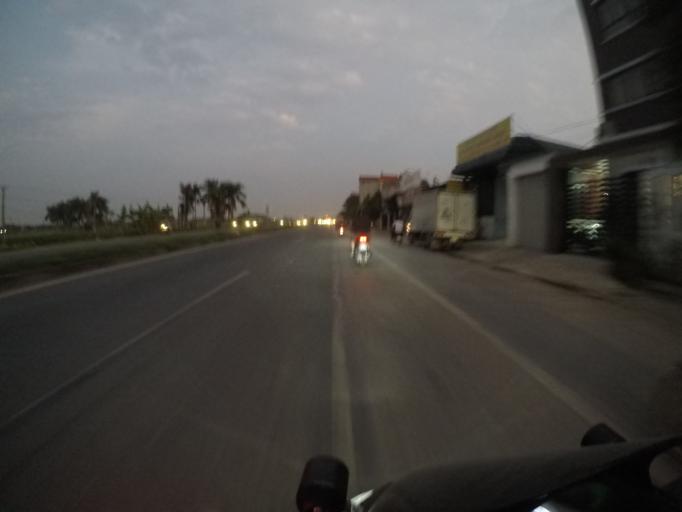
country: VN
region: Vinh Phuc
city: Phuc Yen
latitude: 21.2368
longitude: 105.7446
